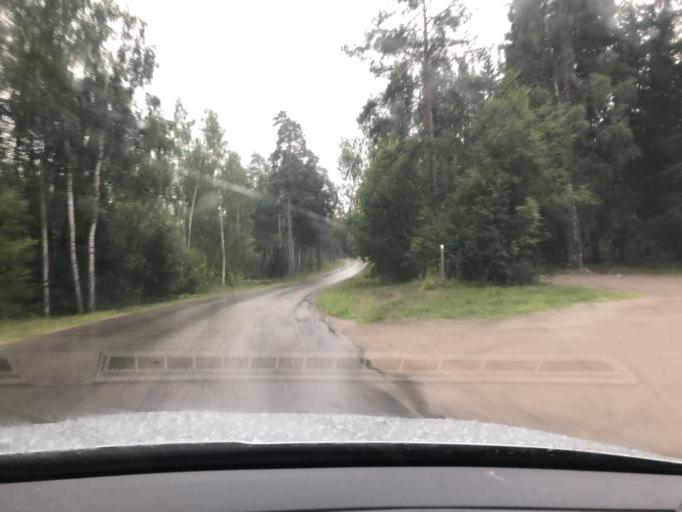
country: SE
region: Vaesternorrland
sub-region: Sundsvalls Kommun
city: Sundsvall
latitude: 62.4034
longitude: 17.3069
